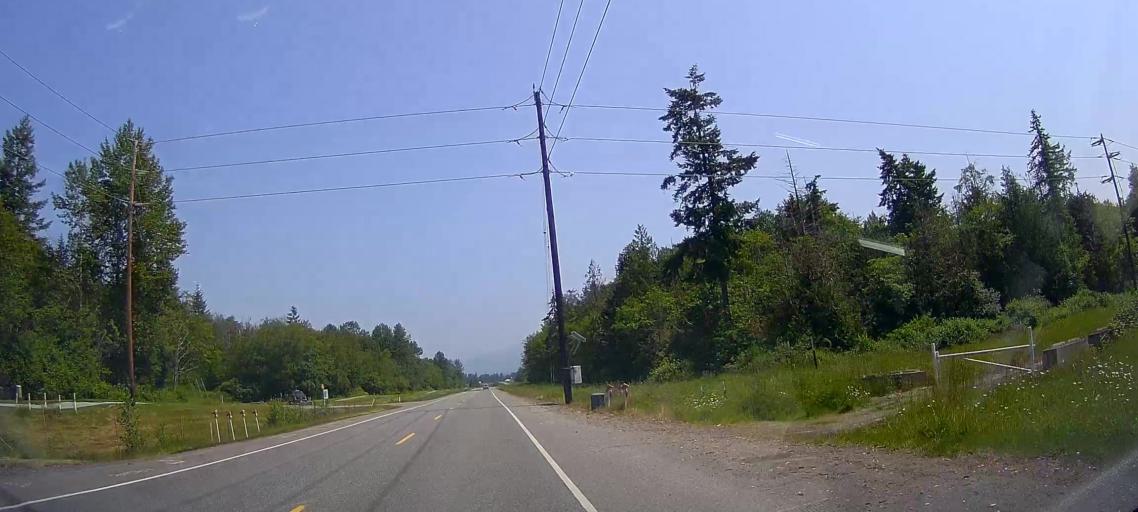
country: US
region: Washington
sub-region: Skagit County
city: Mount Vernon
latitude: 48.4576
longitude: -122.4254
